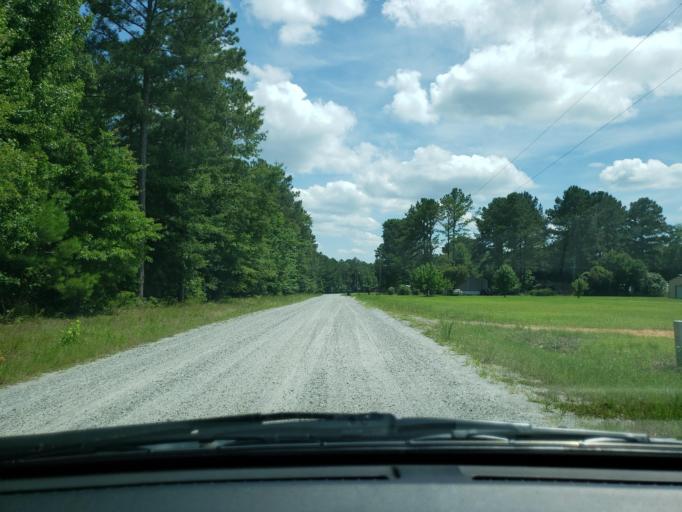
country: US
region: Alabama
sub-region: Elmore County
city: Eclectic
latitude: 32.6278
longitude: -85.9452
